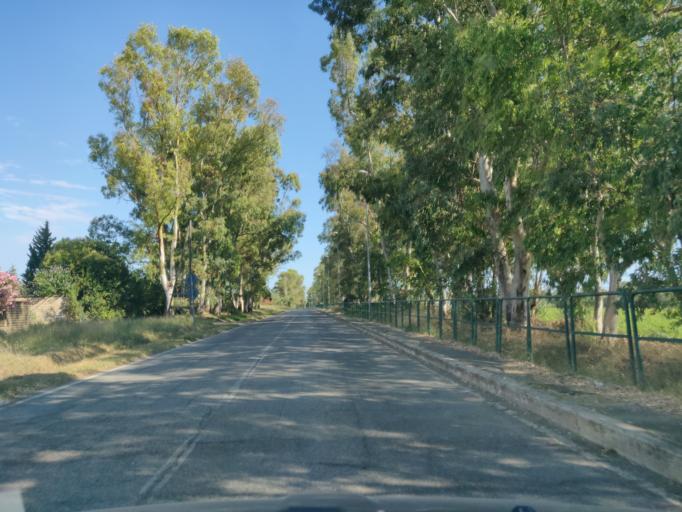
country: IT
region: Latium
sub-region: Citta metropolitana di Roma Capitale
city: Aurelia
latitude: 42.1378
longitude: 11.7680
